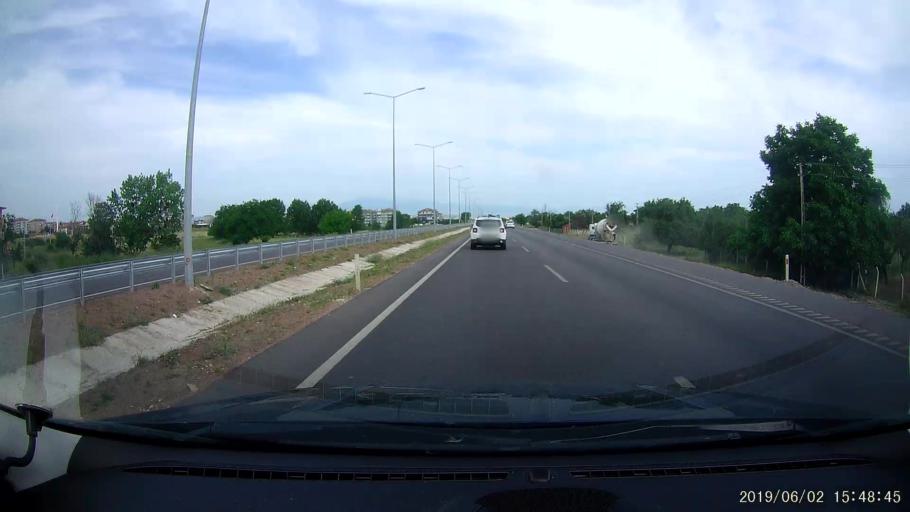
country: TR
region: Amasya
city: Merzifon
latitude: 40.8608
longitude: 35.4479
